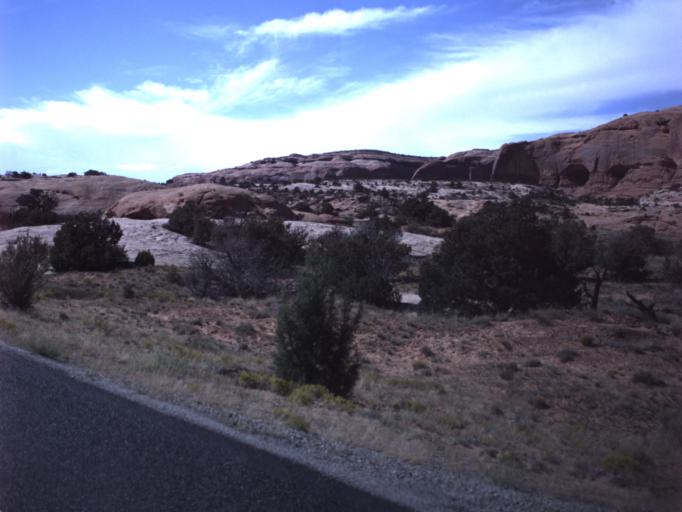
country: US
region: Utah
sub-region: Grand County
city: Moab
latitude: 38.6356
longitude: -109.7770
